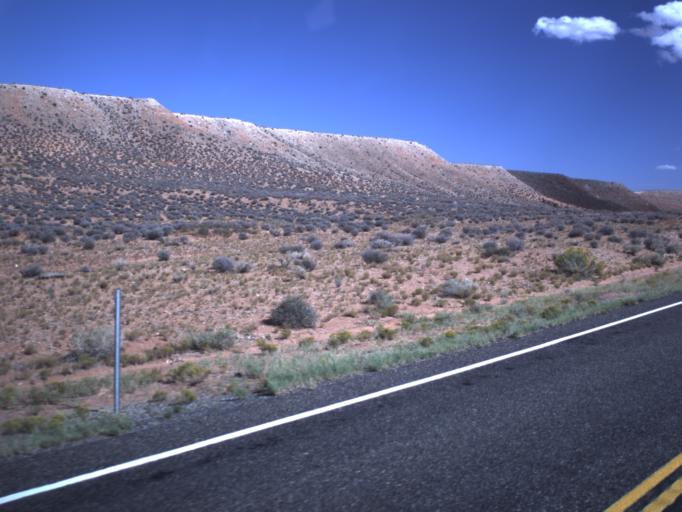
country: US
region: Utah
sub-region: Wayne County
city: Loa
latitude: 38.1483
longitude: -110.6182
